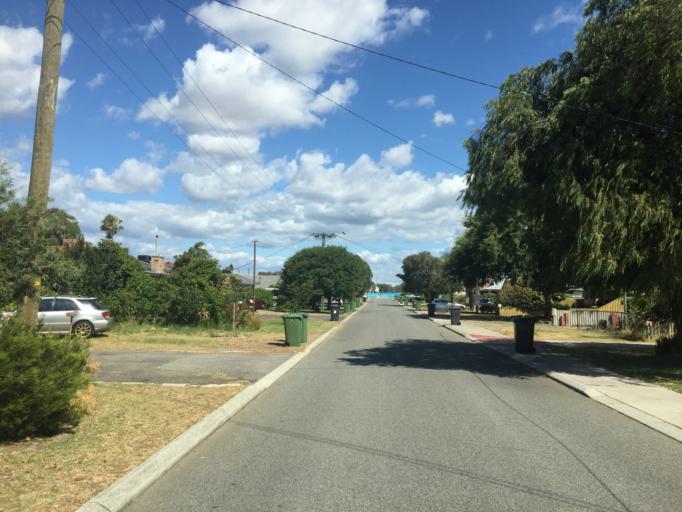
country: AU
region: Western Australia
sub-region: Belmont
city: Redcliffe
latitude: -31.9339
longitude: 115.9464
